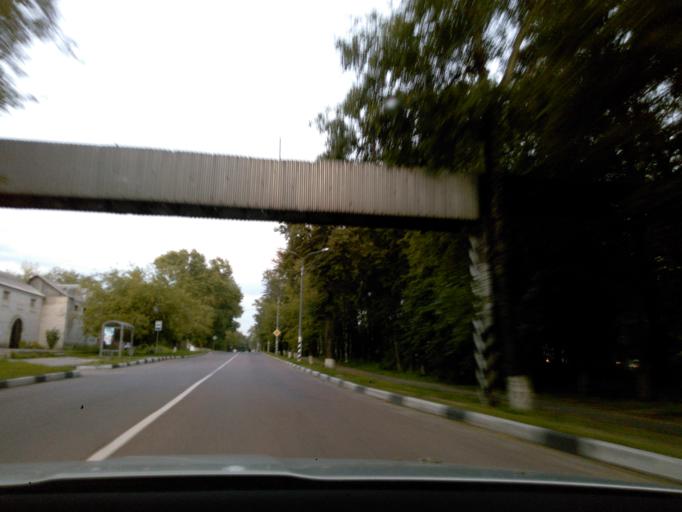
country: RU
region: Moskovskaya
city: Klin
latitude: 56.3400
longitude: 36.7159
